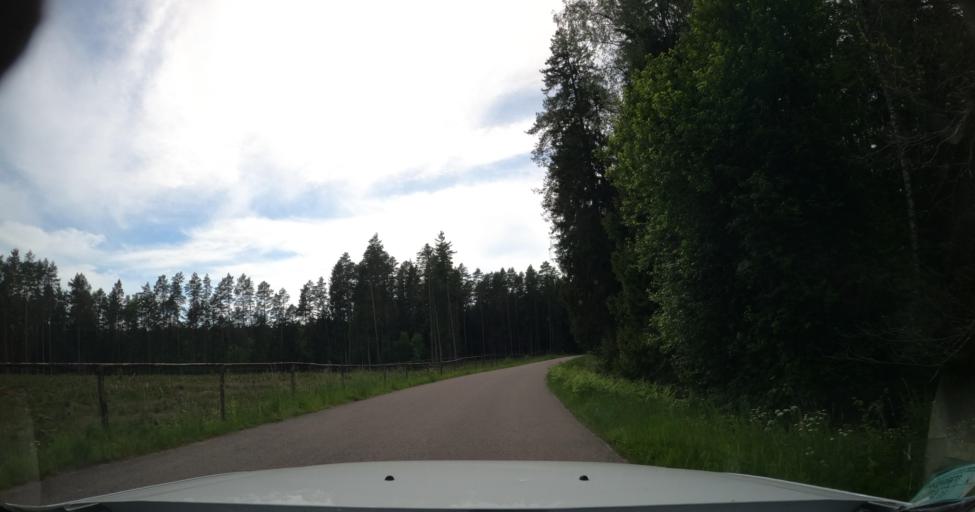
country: PL
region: Warmian-Masurian Voivodeship
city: Dobre Miasto
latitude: 54.1043
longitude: 20.3619
